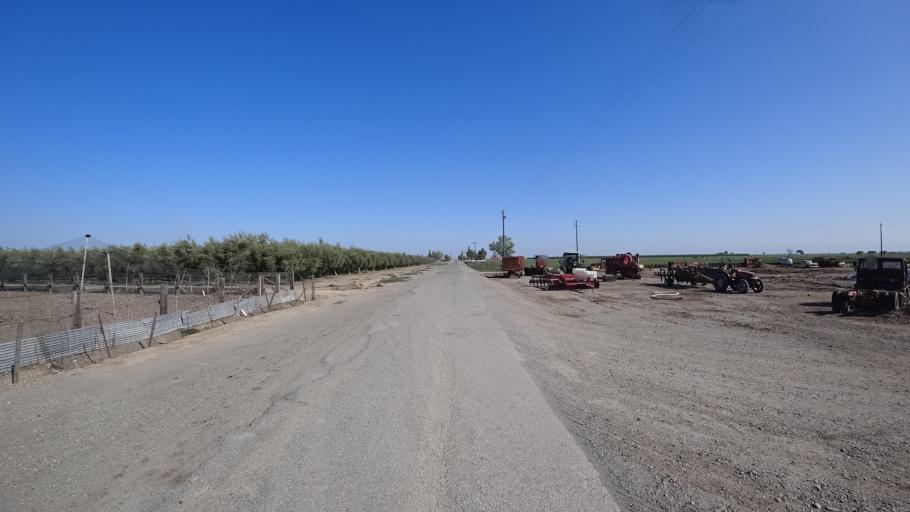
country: US
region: California
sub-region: Glenn County
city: Willows
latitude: 39.5919
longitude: -122.0886
